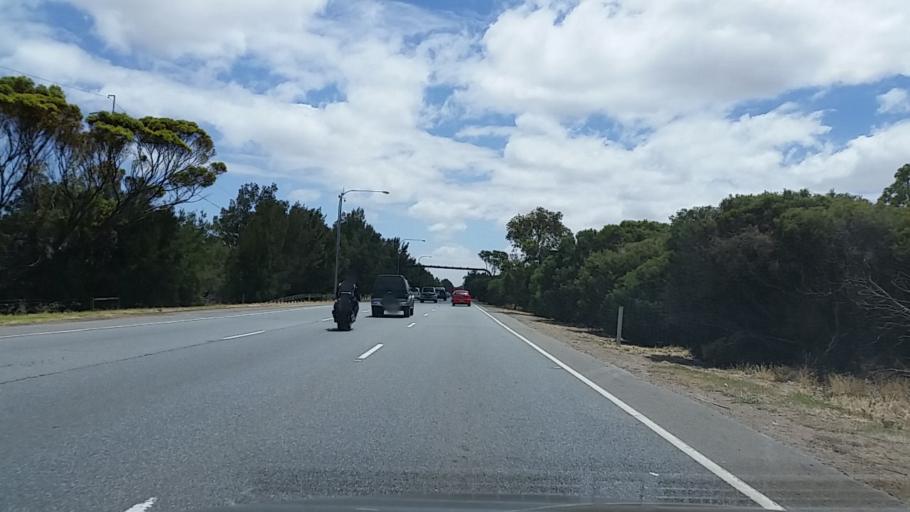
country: AU
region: South Australia
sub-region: Salisbury
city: Ingle Farm
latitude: -34.8088
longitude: 138.5971
